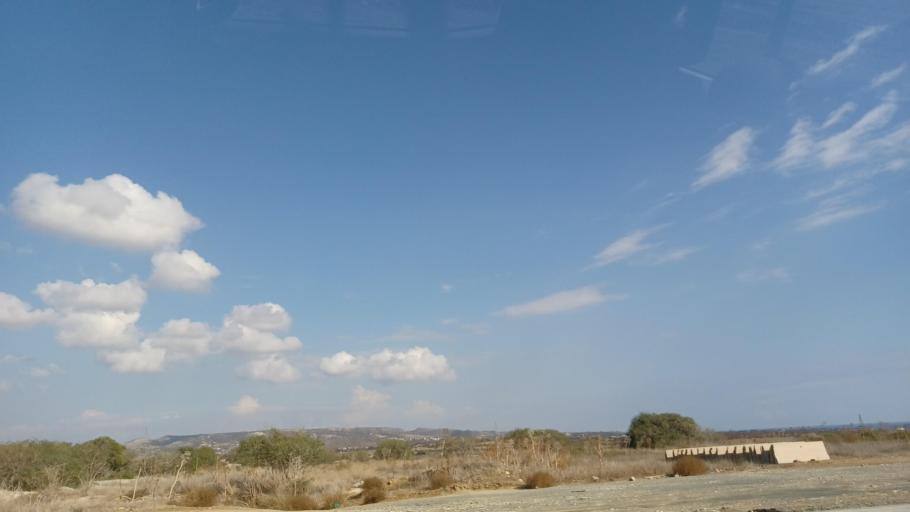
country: CY
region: Limassol
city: Pyrgos
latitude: 34.7305
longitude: 33.3044
